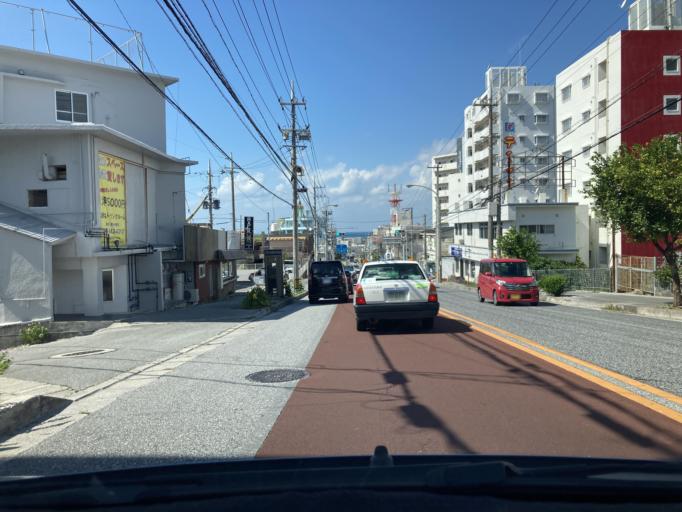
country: JP
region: Okinawa
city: Ginowan
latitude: 26.2659
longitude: 127.7377
